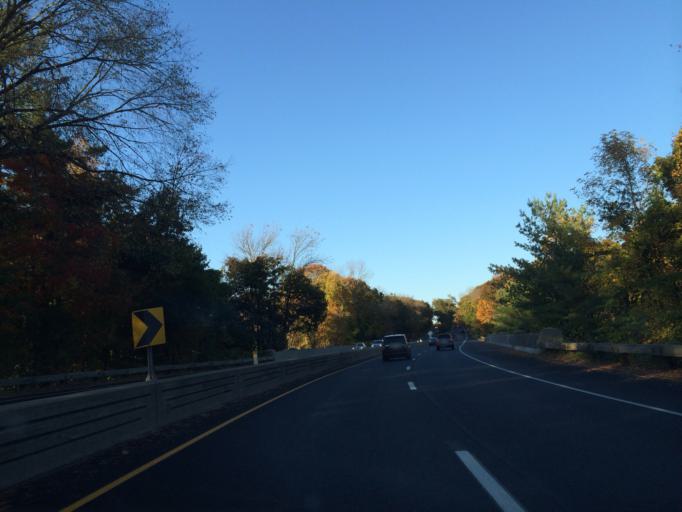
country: US
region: Connecticut
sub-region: Fairfield County
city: Glenville
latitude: 41.0603
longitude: -73.6752
